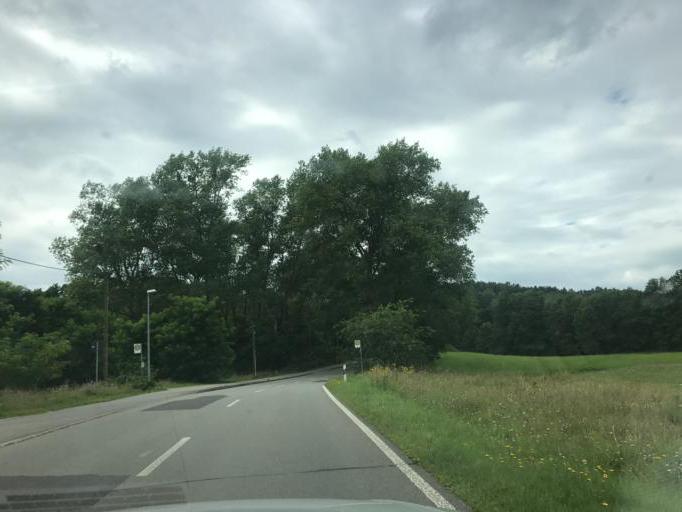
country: DE
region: Mecklenburg-Vorpommern
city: Rechlin
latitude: 53.2470
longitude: 12.6705
